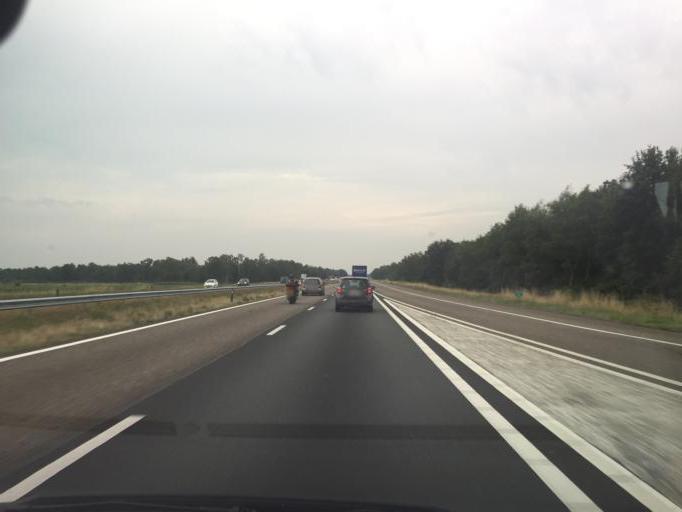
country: NL
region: North Brabant
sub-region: Gemeente Asten
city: Asten
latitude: 51.3900
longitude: 5.8688
